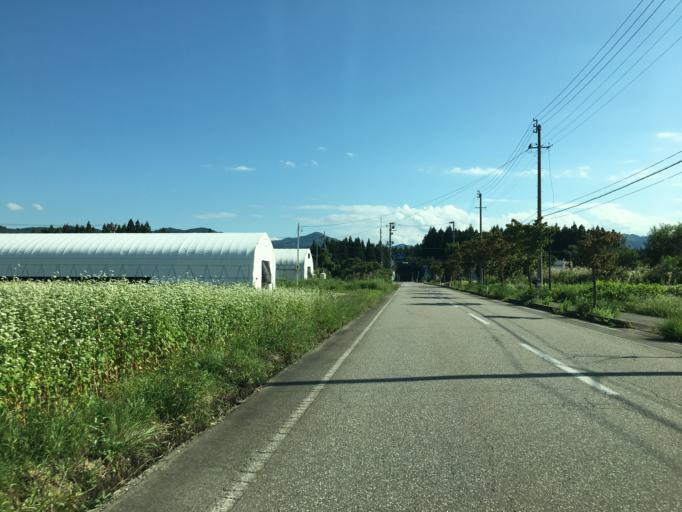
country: JP
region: Fukushima
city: Kitakata
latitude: 37.5983
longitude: 139.6529
